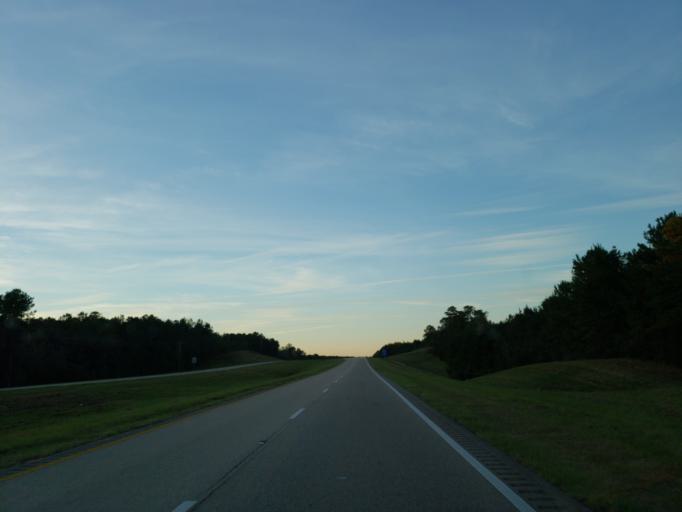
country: US
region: Mississippi
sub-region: Wayne County
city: Belmont
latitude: 31.4785
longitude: -88.4824
